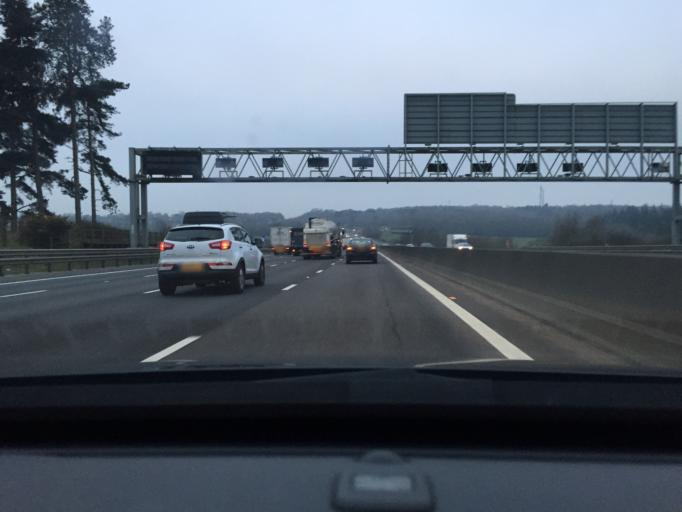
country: GB
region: England
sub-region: Southampton
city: Southampton
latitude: 50.9598
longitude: -1.4356
